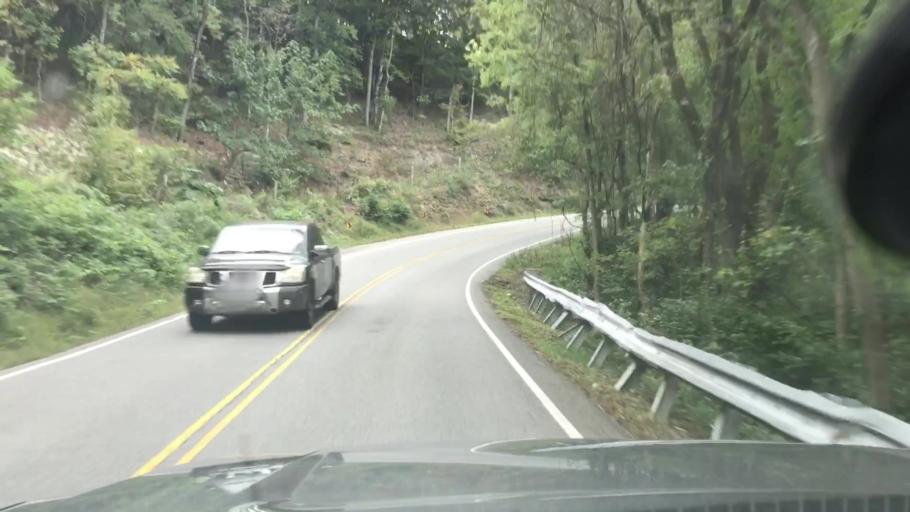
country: US
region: Tennessee
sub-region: Williamson County
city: Brentwood Estates
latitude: 35.9925
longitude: -86.8286
